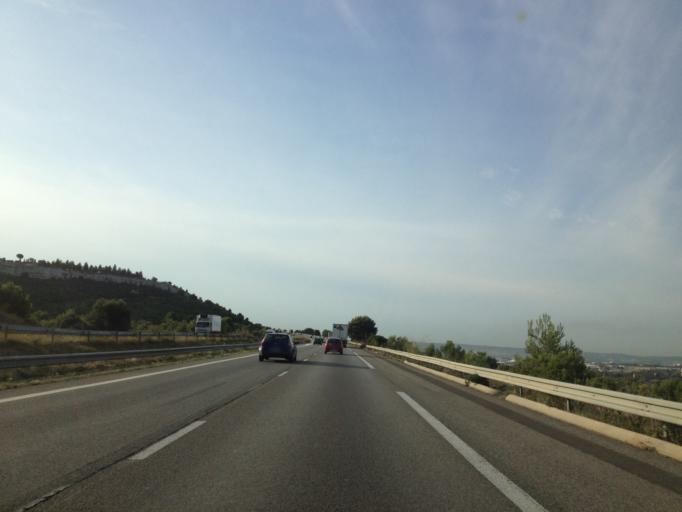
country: FR
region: Provence-Alpes-Cote d'Azur
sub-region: Departement des Bouches-du-Rhone
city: Vitrolles
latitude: 43.4613
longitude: 5.2347
